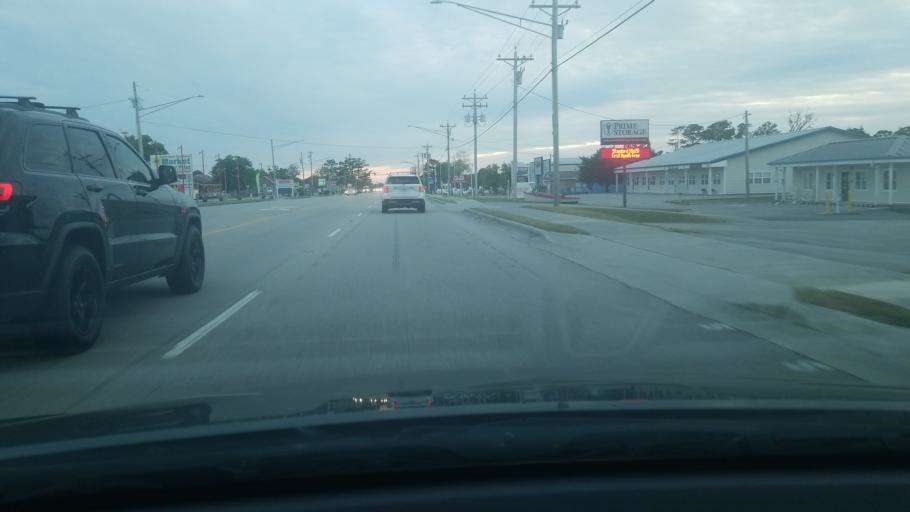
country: US
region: North Carolina
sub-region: Carteret County
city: Cedar Point
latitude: 34.6836
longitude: -77.0828
